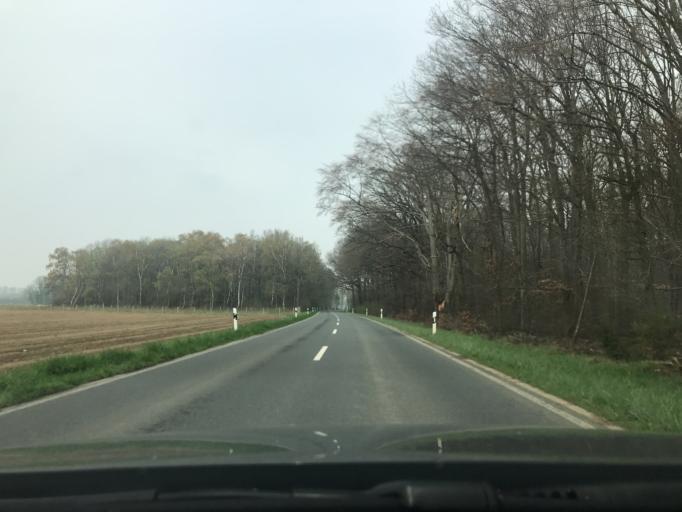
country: DE
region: North Rhine-Westphalia
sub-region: Regierungsbezirk Dusseldorf
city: Wachtendonk
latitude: 51.4465
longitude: 6.3329
